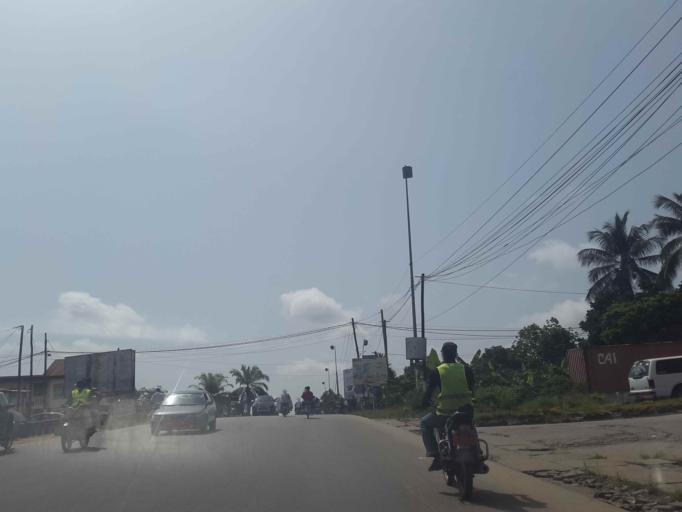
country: CM
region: Littoral
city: Douala
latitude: 4.0843
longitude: 9.7377
